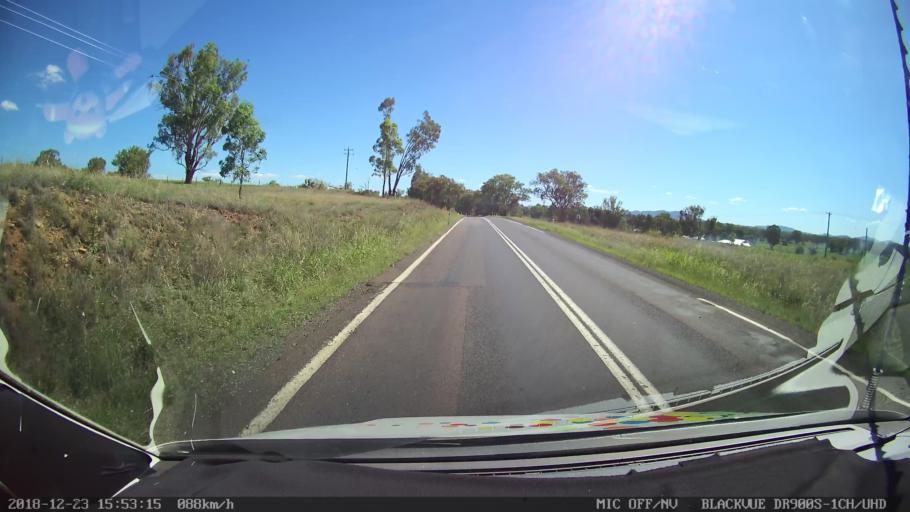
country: AU
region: New South Wales
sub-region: Tamworth Municipality
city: Phillip
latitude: -31.1309
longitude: 150.8823
